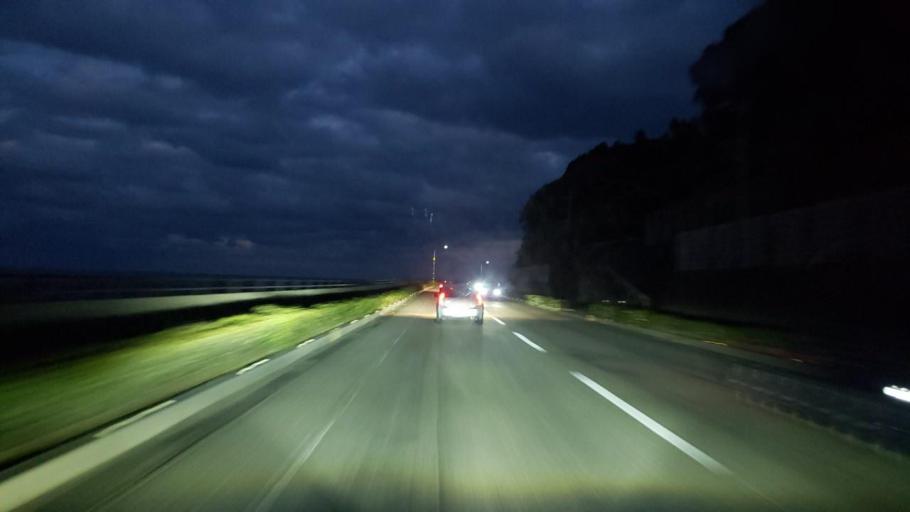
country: JP
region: Tokushima
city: Narutocho-mitsuishi
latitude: 34.2226
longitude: 134.4928
